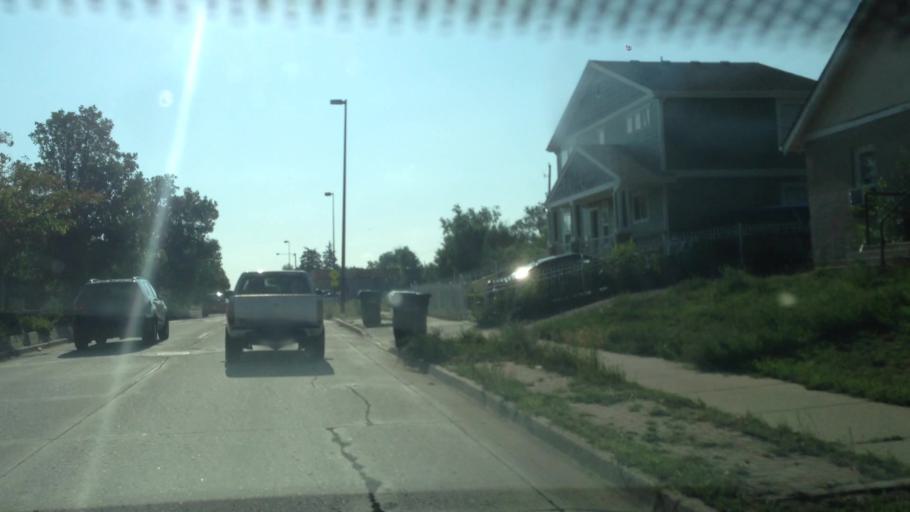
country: US
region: Colorado
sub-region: Jefferson County
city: Lakewood
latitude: 39.7112
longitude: -105.0455
